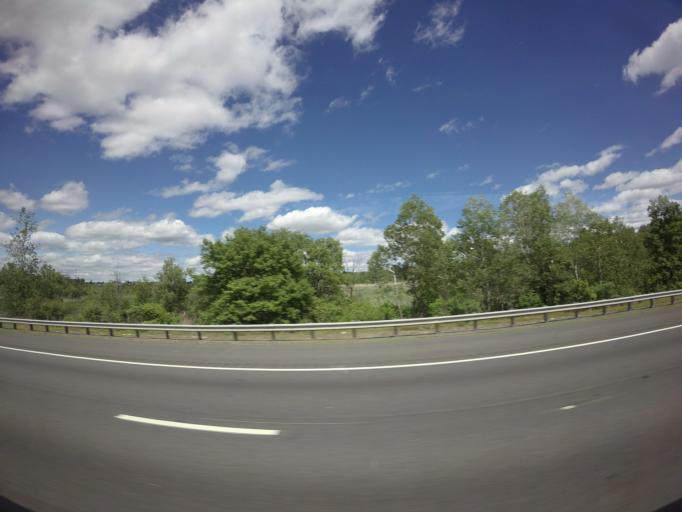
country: US
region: Massachusetts
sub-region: Middlesex County
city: Wilmington
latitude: 42.5506
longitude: -71.1369
